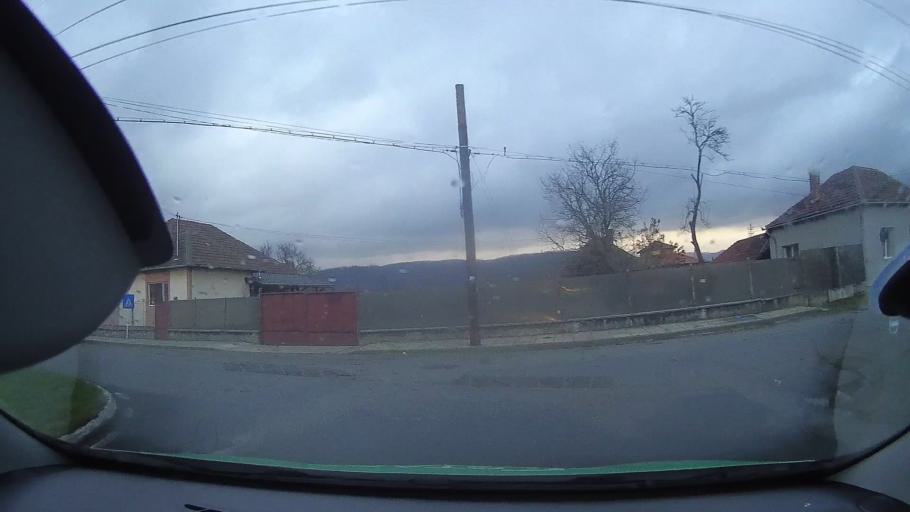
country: RO
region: Hunedoara
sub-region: Comuna Baia de Cris
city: Baia de Cris
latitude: 46.1735
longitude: 22.7152
